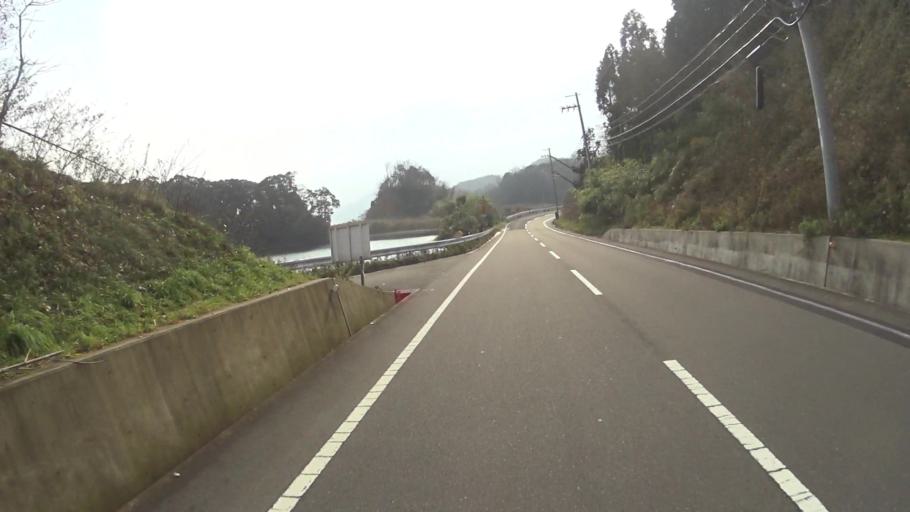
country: JP
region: Kyoto
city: Maizuru
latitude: 35.4844
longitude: 135.3241
